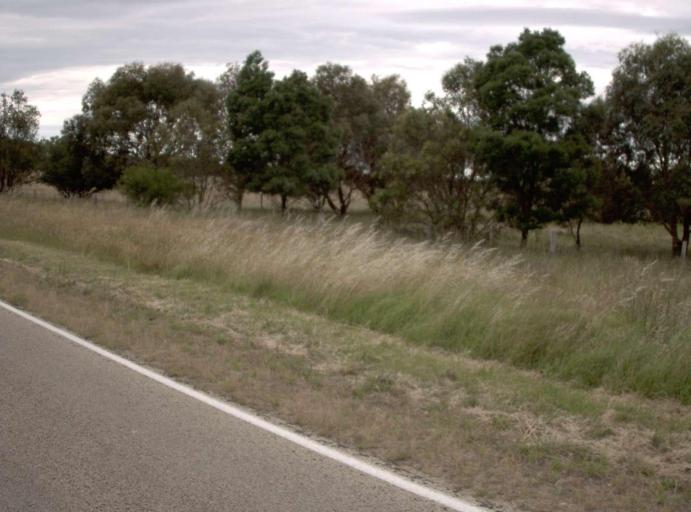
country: AU
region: Victoria
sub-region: East Gippsland
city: Bairnsdale
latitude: -37.9757
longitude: 147.4649
